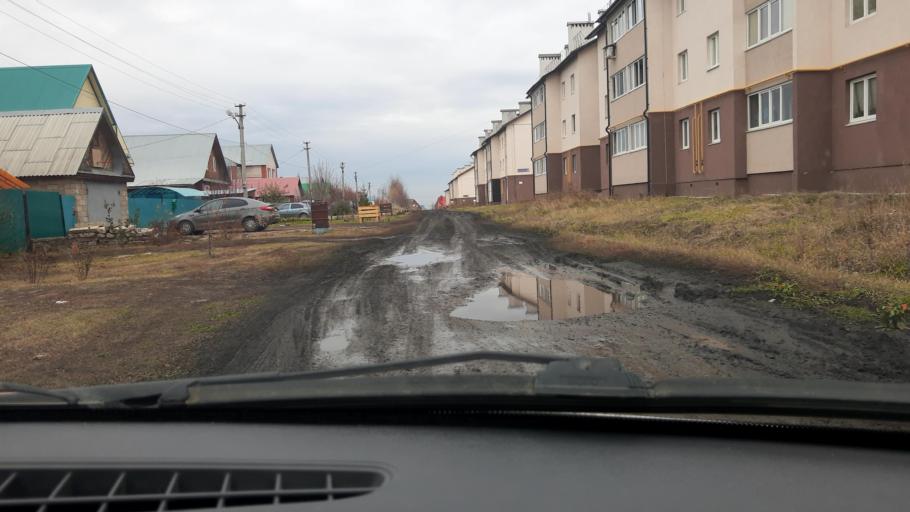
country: RU
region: Bashkortostan
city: Avdon
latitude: 54.6956
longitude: 55.8021
